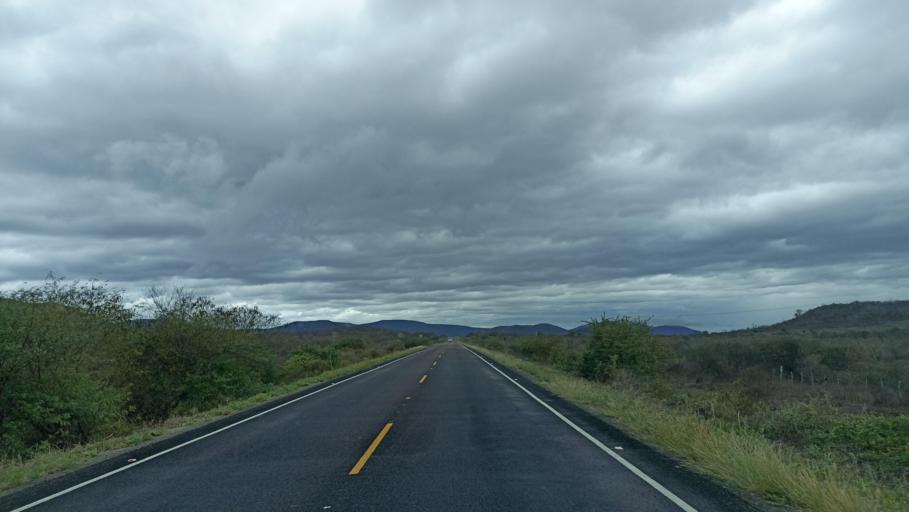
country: BR
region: Bahia
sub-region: Iacu
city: Iacu
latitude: -12.9048
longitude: -40.4048
